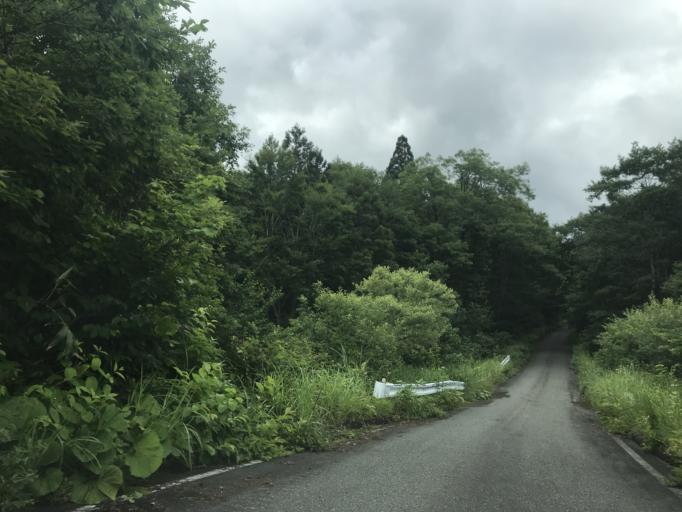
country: JP
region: Iwate
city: Ichinoseki
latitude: 38.9357
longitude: 140.8778
